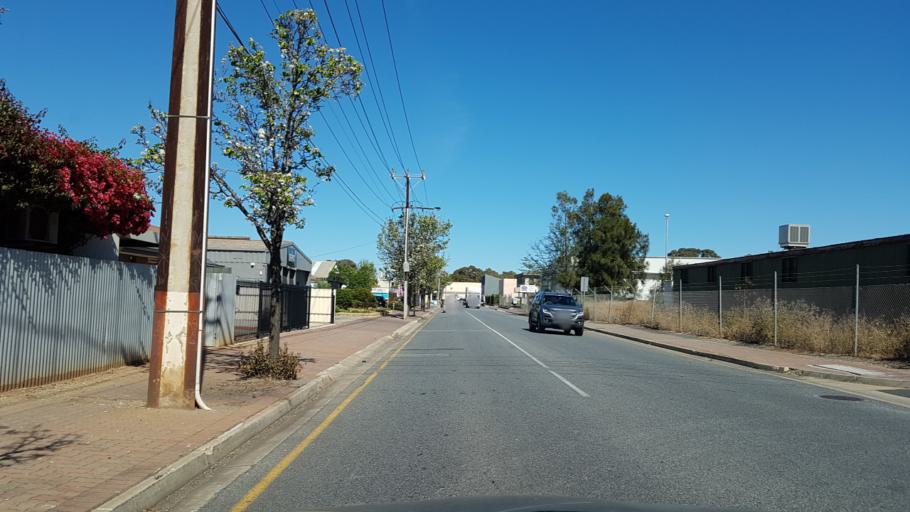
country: AU
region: South Australia
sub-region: City of West Torrens
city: Thebarton
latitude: -34.9147
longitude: 138.5566
